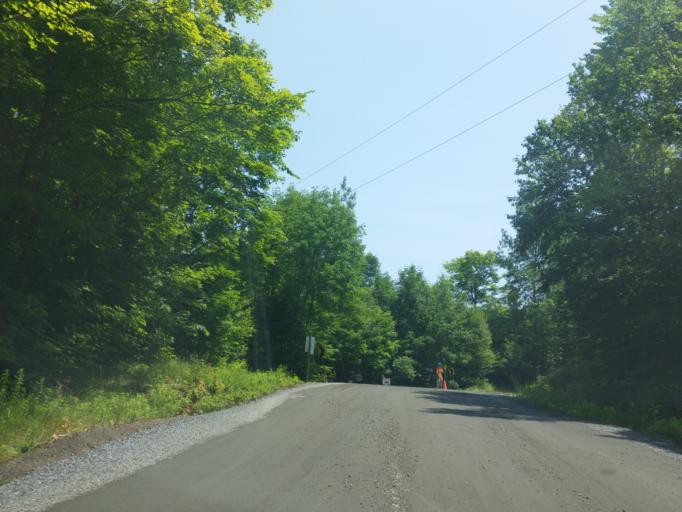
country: CA
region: Ontario
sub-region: Parry Sound District
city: Parry Sound
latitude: 45.4451
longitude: -80.0062
